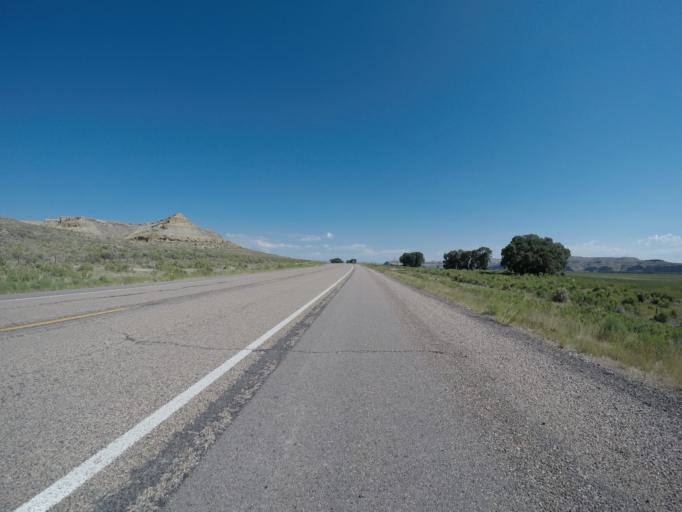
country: US
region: Wyoming
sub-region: Sublette County
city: Marbleton
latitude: 42.1974
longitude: -110.1785
